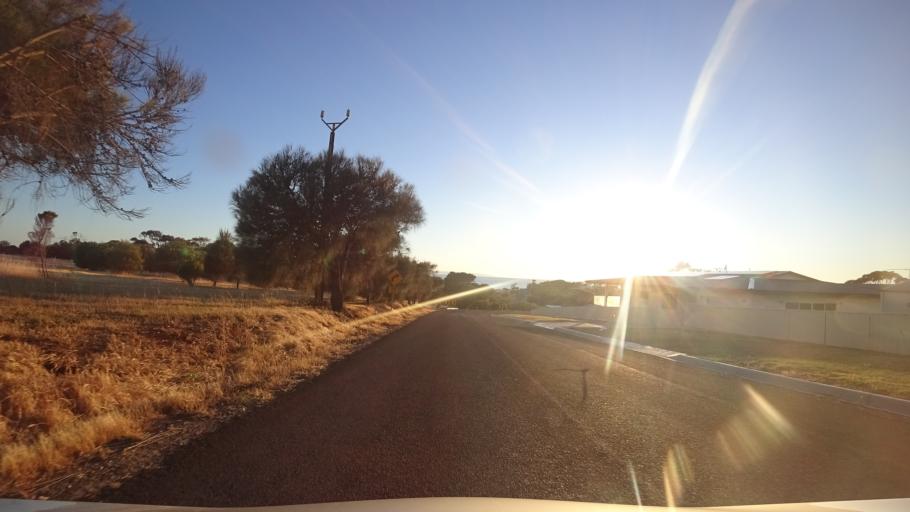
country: AU
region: South Australia
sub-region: Kangaroo Island
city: Kingscote
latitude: -35.6456
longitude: 137.6344
